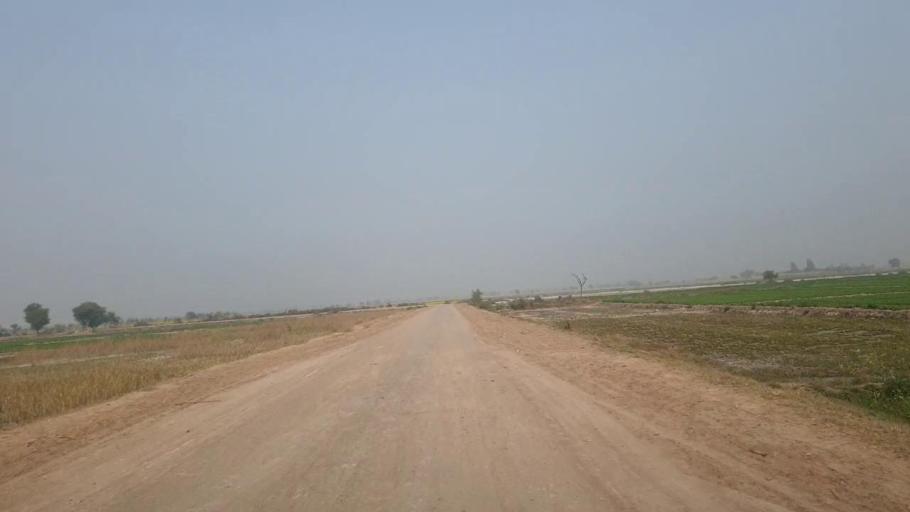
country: PK
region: Sindh
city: Shahdadpur
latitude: 25.8432
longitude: 68.5789
